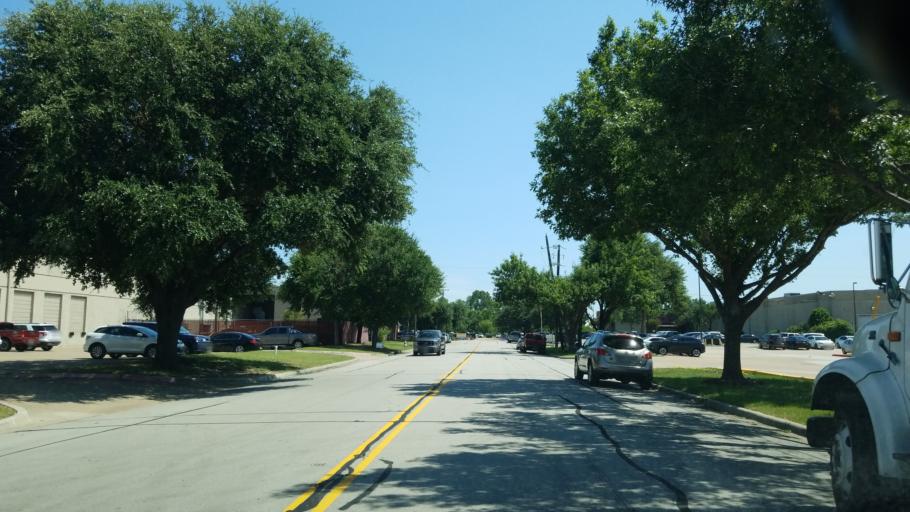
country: US
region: Texas
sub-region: Dallas County
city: Farmers Branch
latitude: 32.9182
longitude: -96.9054
